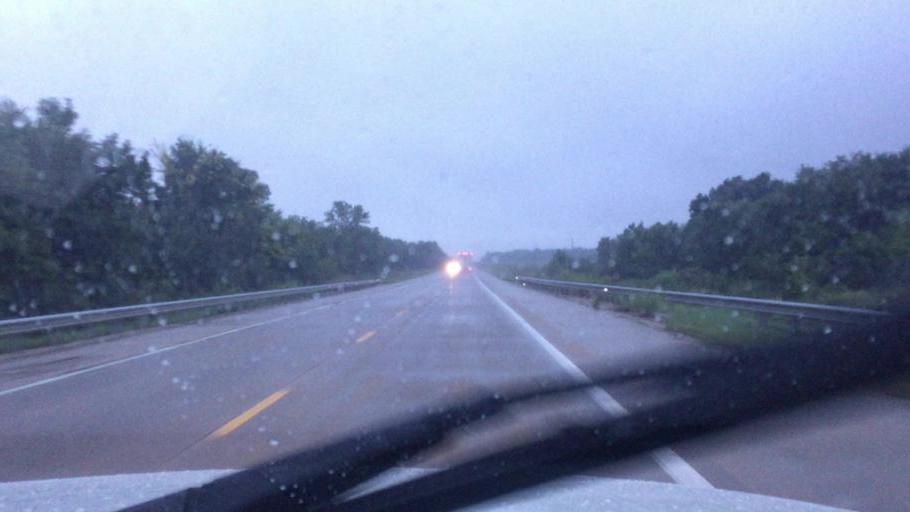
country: US
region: Kansas
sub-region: Neosho County
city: Chanute
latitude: 37.5577
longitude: -95.4709
